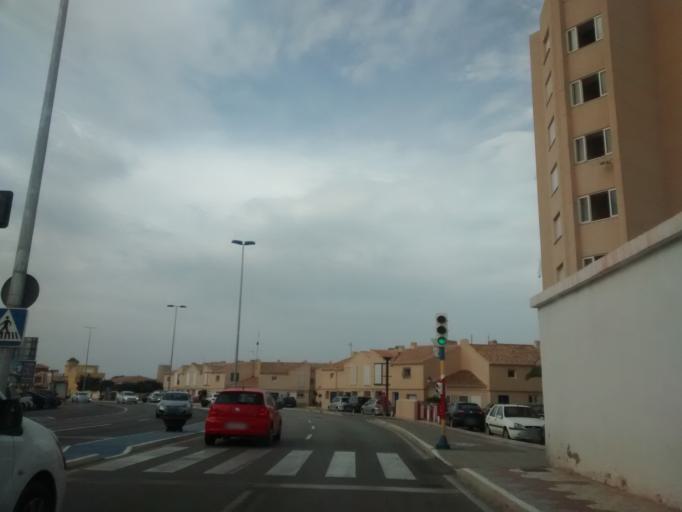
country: ES
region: Murcia
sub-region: Murcia
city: La Manga del Mar Menor
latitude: 37.6733
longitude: -0.7305
